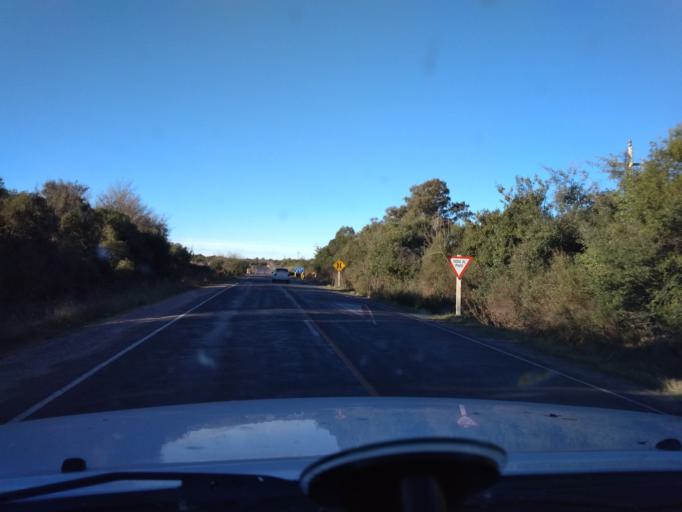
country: UY
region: Canelones
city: San Ramon
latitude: -34.2713
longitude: -55.9434
